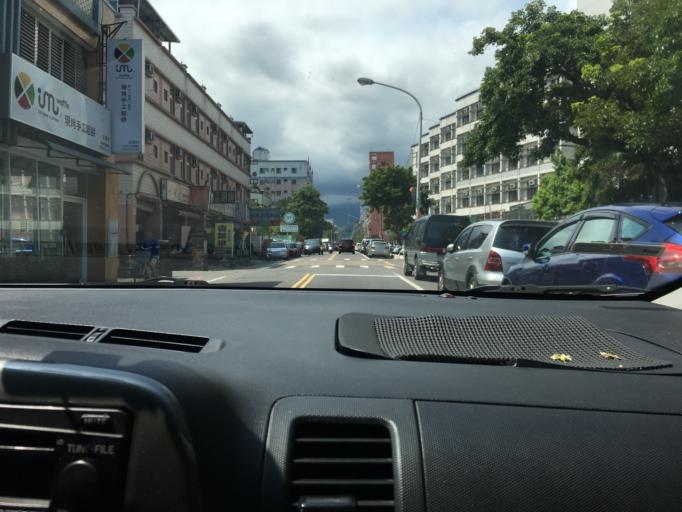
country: TW
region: Taiwan
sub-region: Yilan
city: Yilan
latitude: 24.7450
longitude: 121.7443
